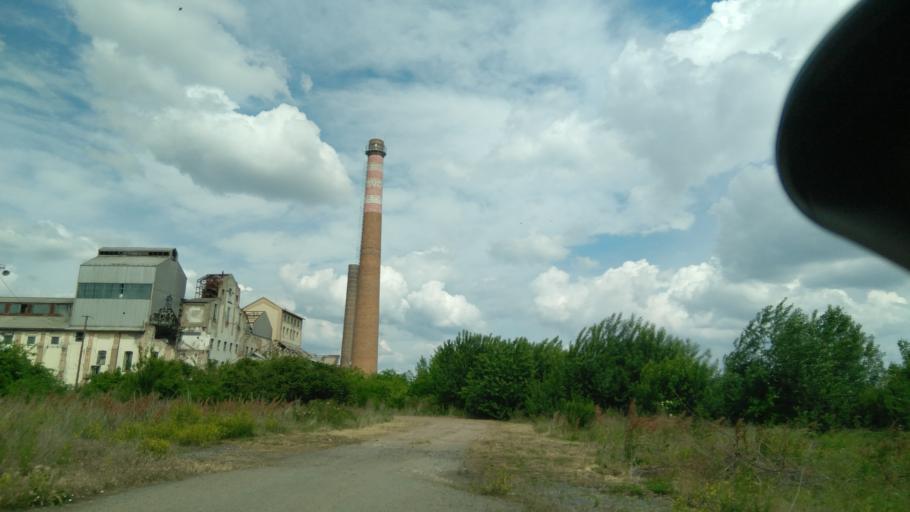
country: HU
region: Bekes
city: Mezohegyes
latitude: 46.3086
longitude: 20.8068
